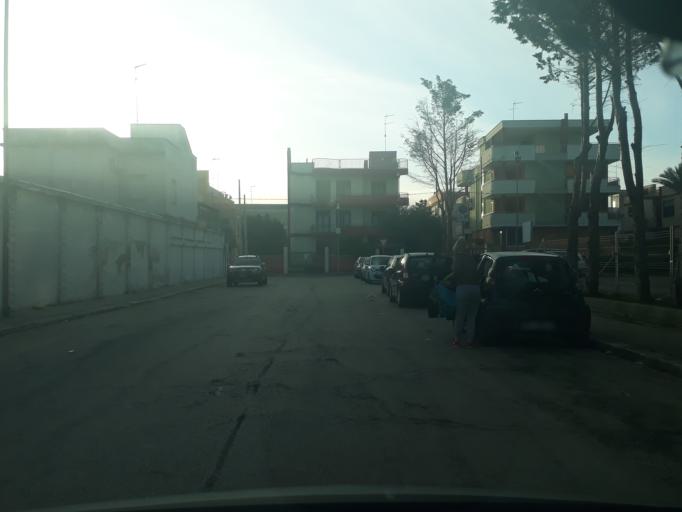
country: IT
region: Apulia
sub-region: Provincia di Brindisi
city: Brindisi
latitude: 40.6483
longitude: 17.9378
